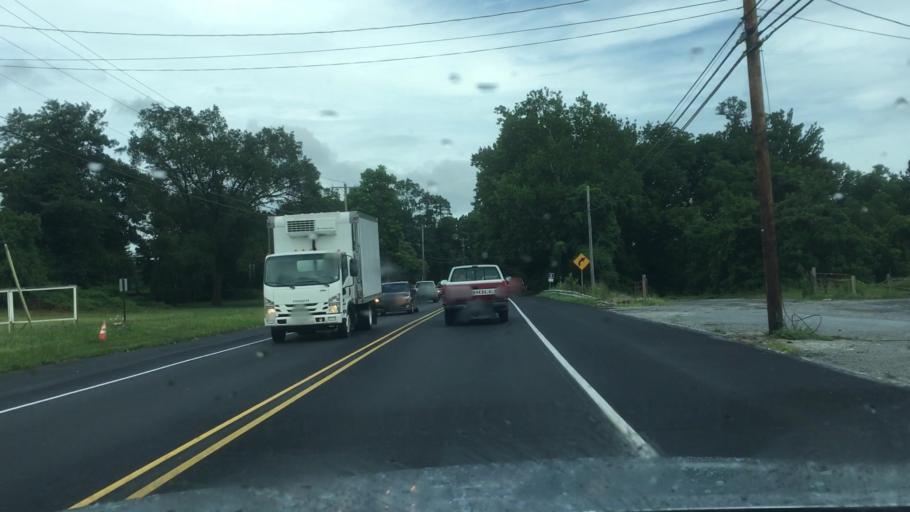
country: US
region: Pennsylvania
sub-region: Chester County
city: Avondale
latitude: 39.8317
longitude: -75.7886
